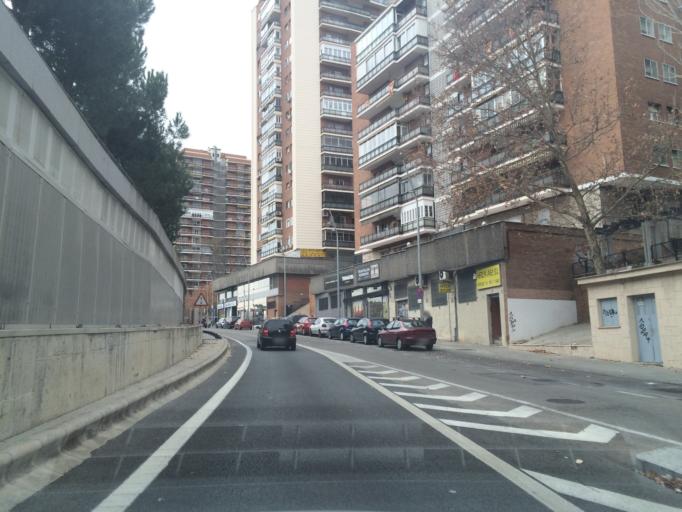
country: ES
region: Madrid
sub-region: Provincia de Madrid
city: City Center
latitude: 40.4154
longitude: -3.7238
